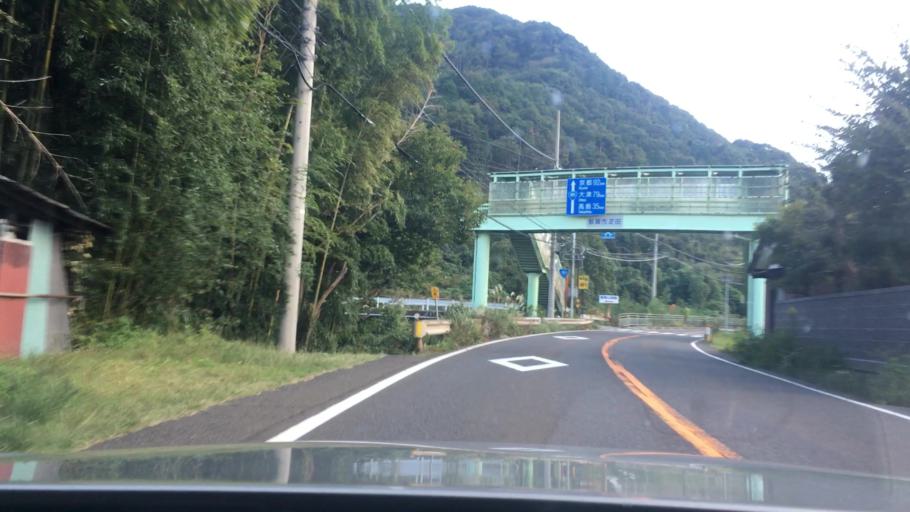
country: JP
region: Fukui
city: Tsuruga
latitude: 35.6012
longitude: 136.1015
